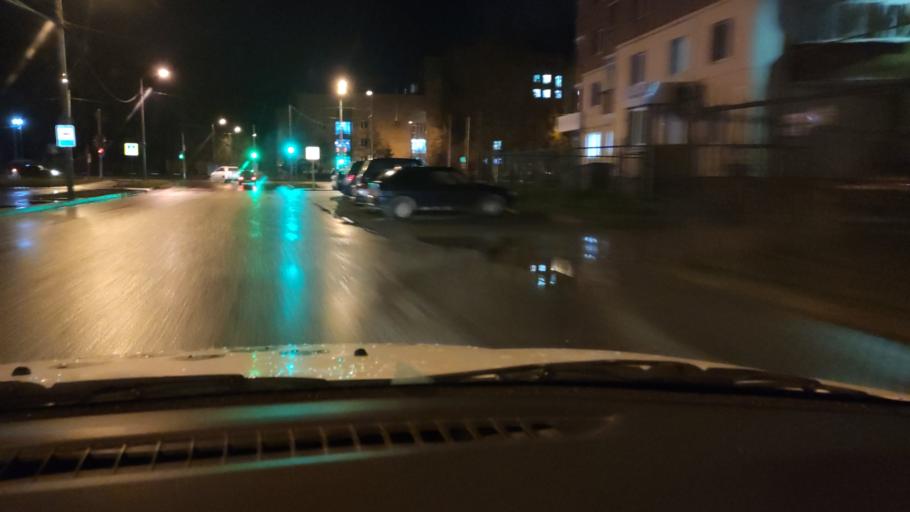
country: RU
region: Perm
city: Kondratovo
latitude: 57.9936
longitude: 56.1483
